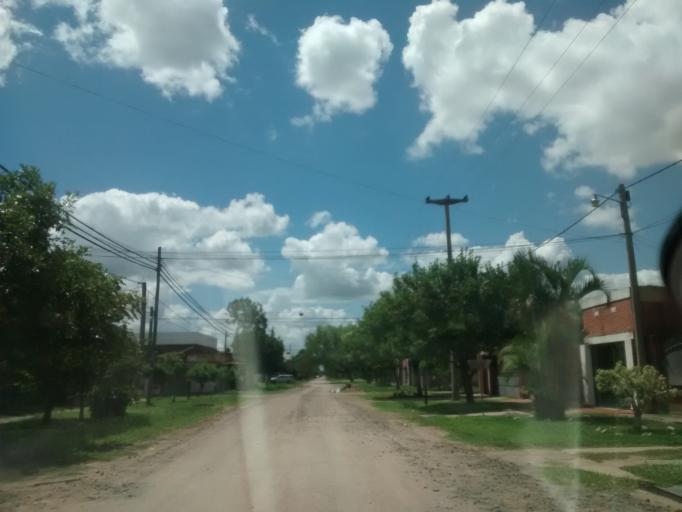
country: AR
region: Chaco
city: Resistencia
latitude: -27.4625
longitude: -59.0114
